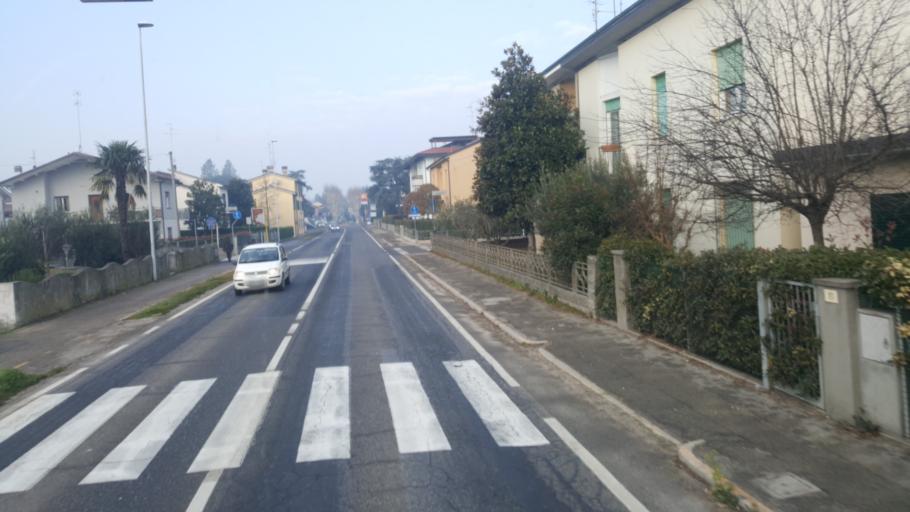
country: IT
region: Emilia-Romagna
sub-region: Provincia di Ravenna
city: Bagnacavallo
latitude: 44.4129
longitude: 11.9858
